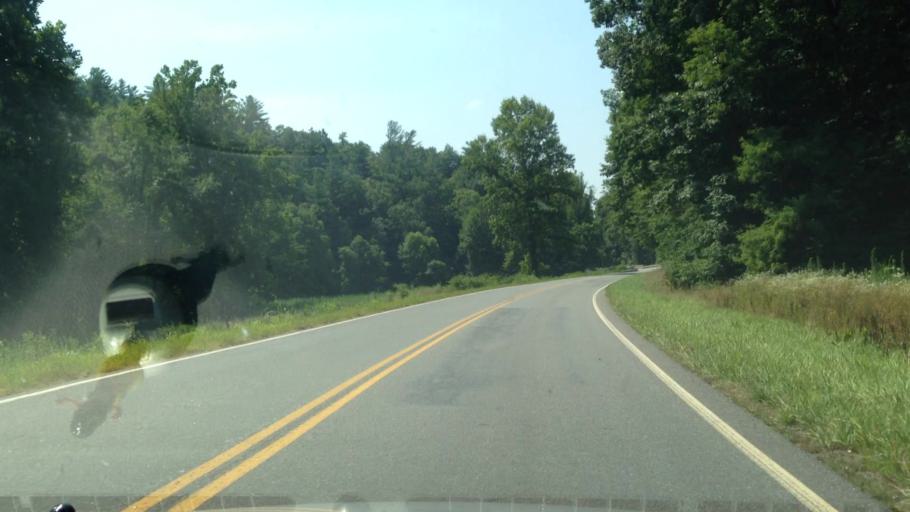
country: US
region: Virginia
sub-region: Patrick County
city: Stuart
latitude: 36.5806
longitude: -80.3813
